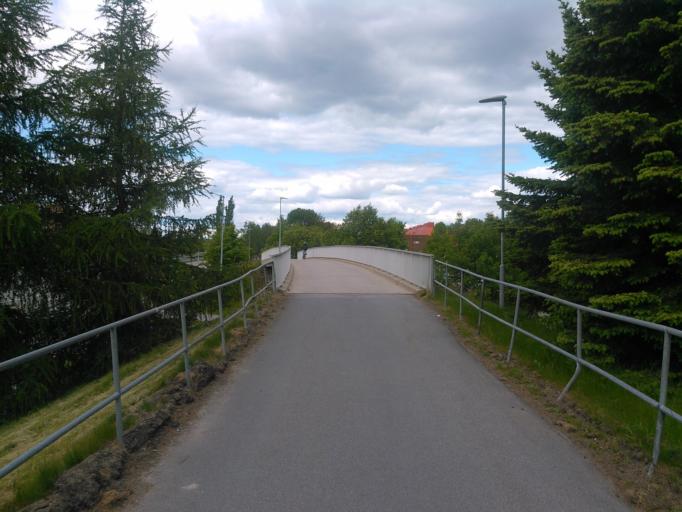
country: SE
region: Vaesterbotten
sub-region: Umea Kommun
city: Umea
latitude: 63.8216
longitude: 20.2930
